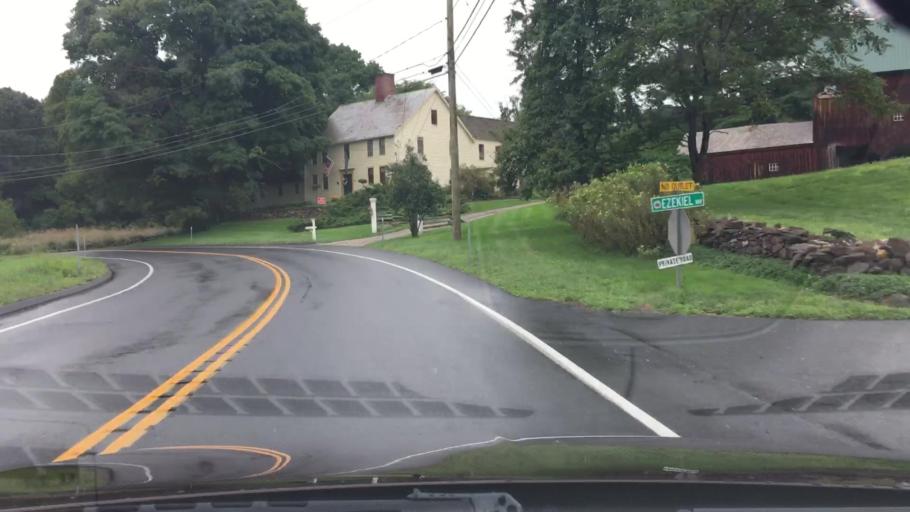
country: US
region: Connecticut
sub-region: Hartford County
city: Tariffville
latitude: 41.9441
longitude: -72.7449
